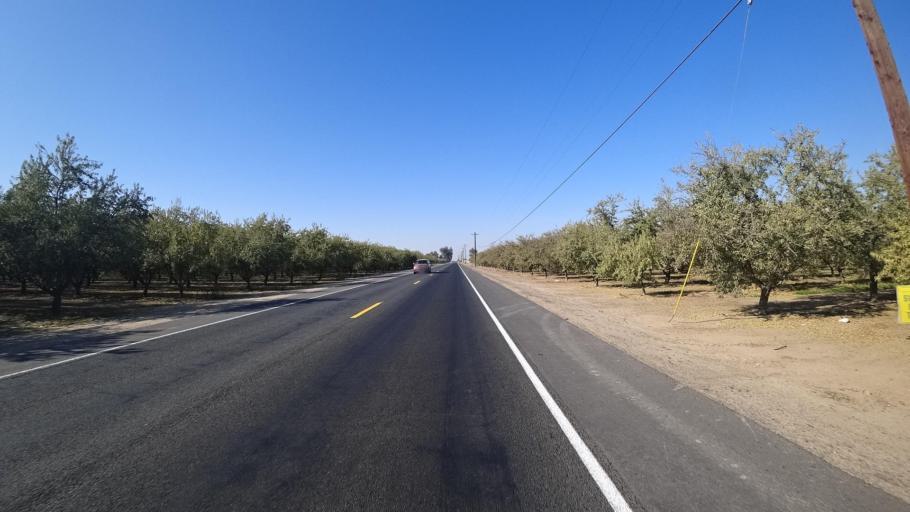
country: US
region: California
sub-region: Kern County
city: Delano
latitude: 35.7177
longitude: -119.3228
